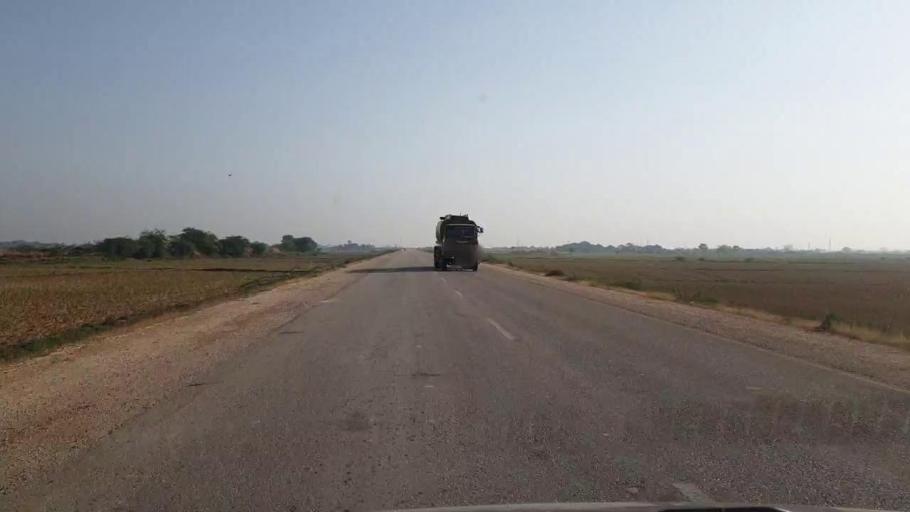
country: PK
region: Sindh
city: Badin
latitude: 24.6745
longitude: 68.8073
